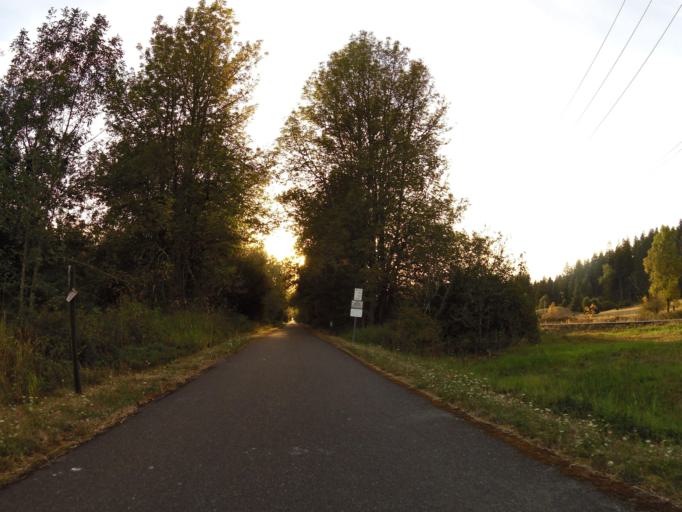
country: US
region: Washington
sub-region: Thurston County
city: Tenino
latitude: 46.8584
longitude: -122.8045
